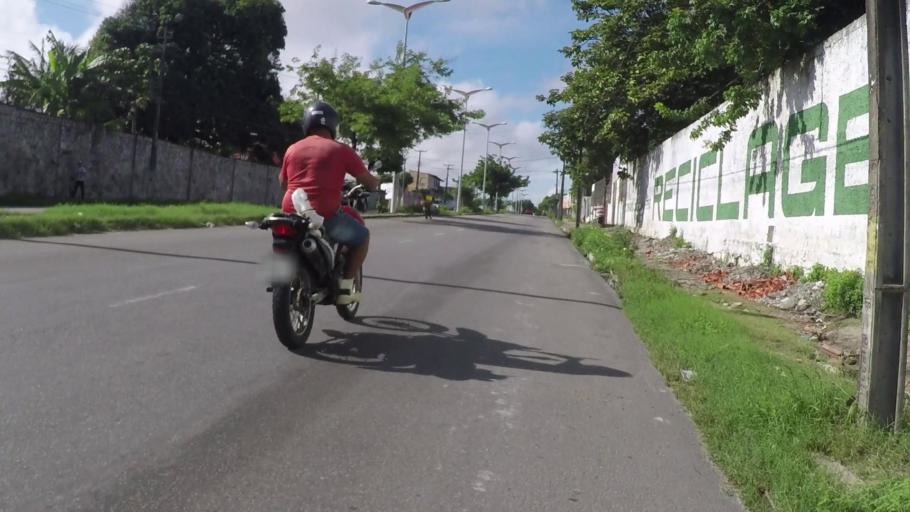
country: BR
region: Ceara
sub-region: Fortaleza
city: Fortaleza
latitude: -3.7039
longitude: -38.5916
